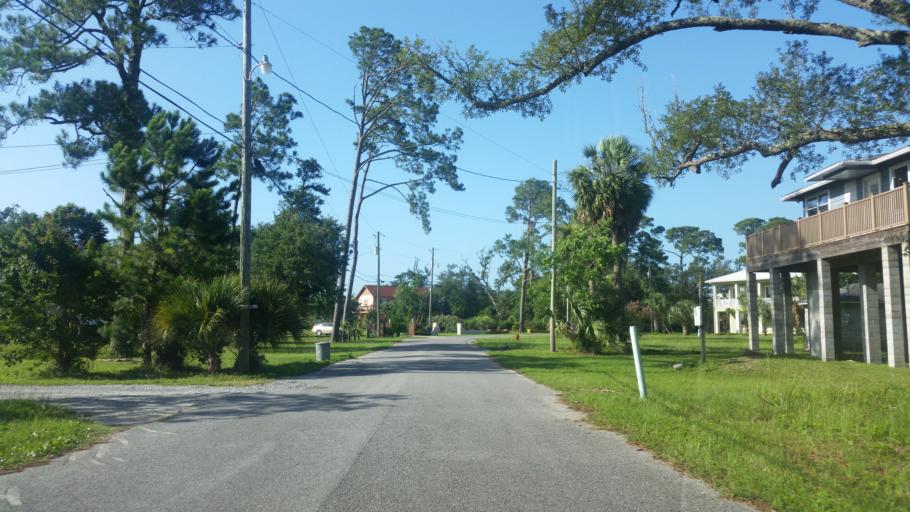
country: US
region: Florida
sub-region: Escambia County
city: Warrington
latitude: 30.3756
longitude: -87.2712
